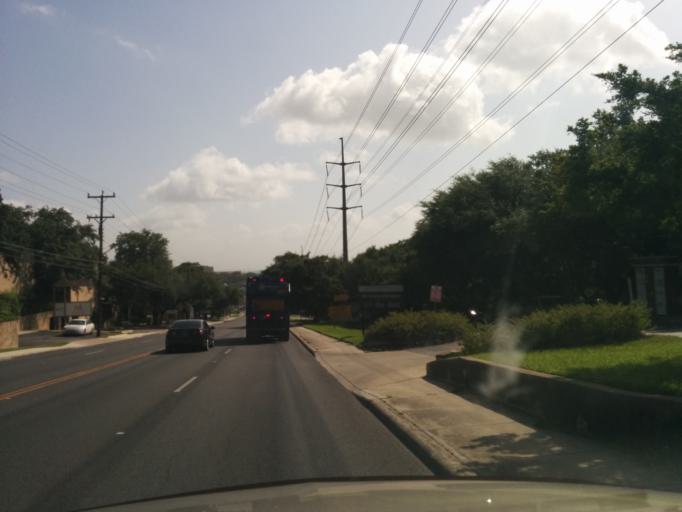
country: US
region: Texas
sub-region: Bexar County
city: Balcones Heights
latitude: 29.5220
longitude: -98.5713
